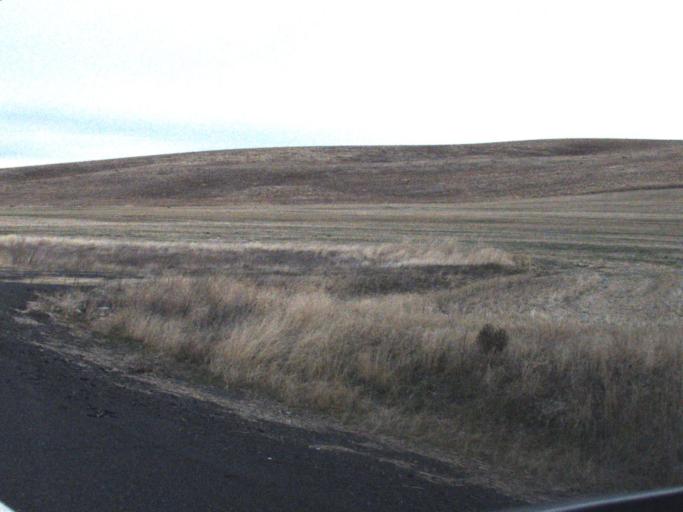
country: US
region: Washington
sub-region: Garfield County
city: Pomeroy
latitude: 46.8022
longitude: -117.8428
